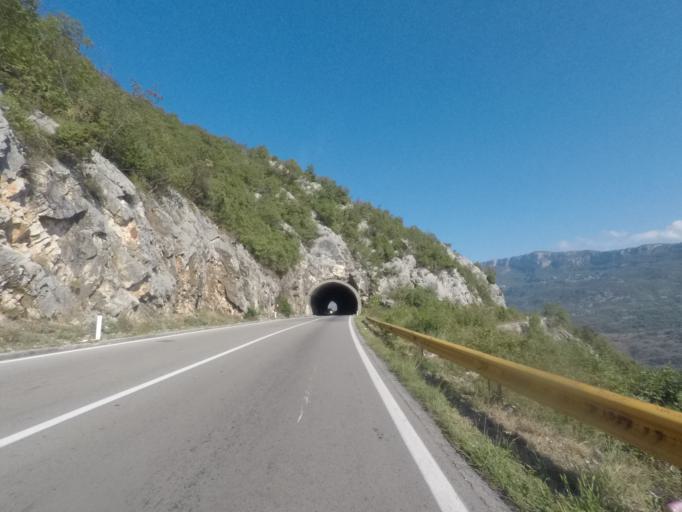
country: ME
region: Opstina Niksic
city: Niksic
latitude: 42.6325
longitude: 19.0070
